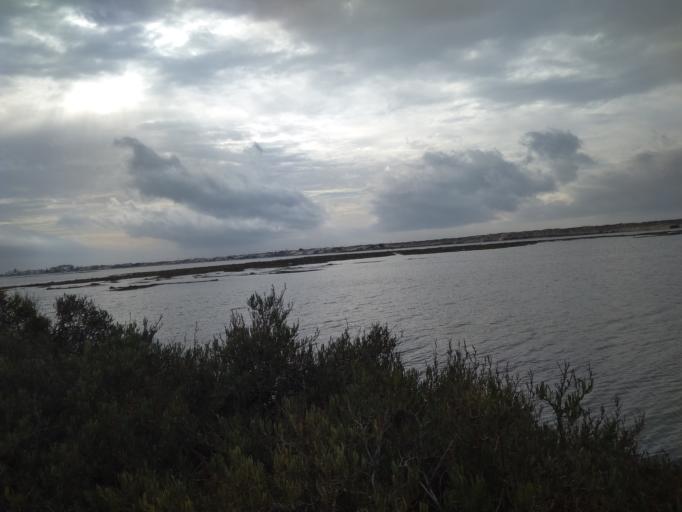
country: PT
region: Faro
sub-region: Loule
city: Almancil
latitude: 37.0207
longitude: -8.0052
